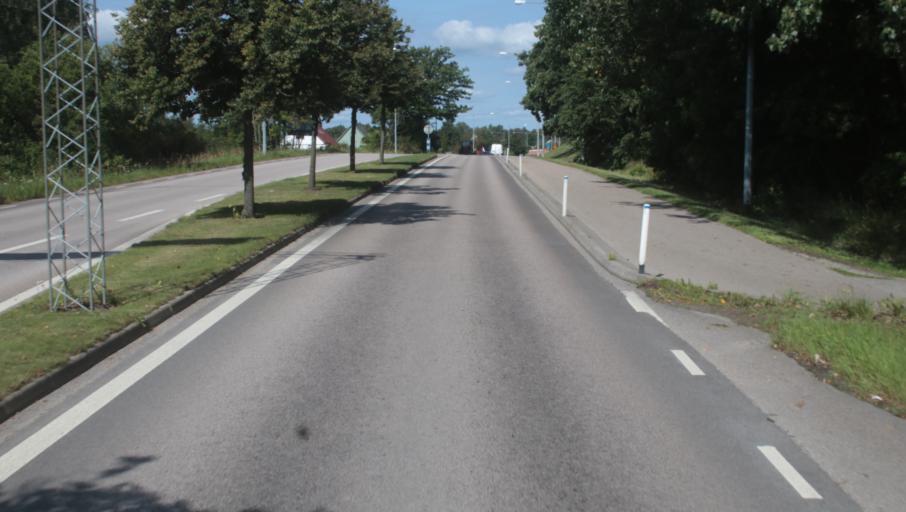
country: SE
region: Blekinge
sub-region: Karlshamns Kommun
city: Karlshamn
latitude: 56.1947
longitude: 14.8414
